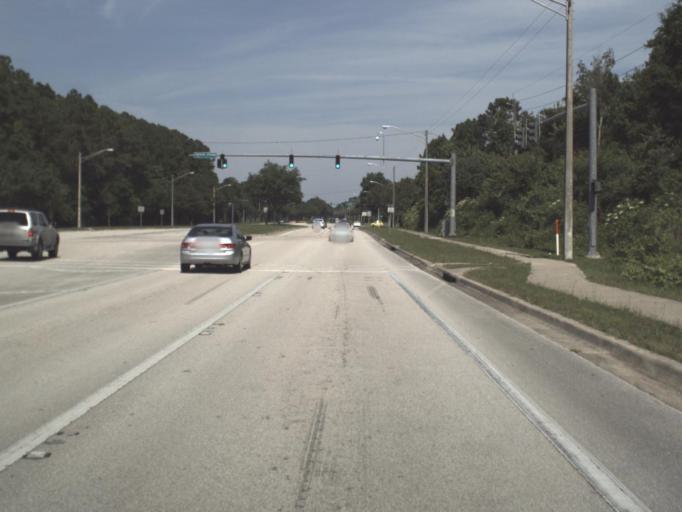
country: US
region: Florida
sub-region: Saint Johns County
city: Fruit Cove
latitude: 30.2153
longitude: -81.5423
